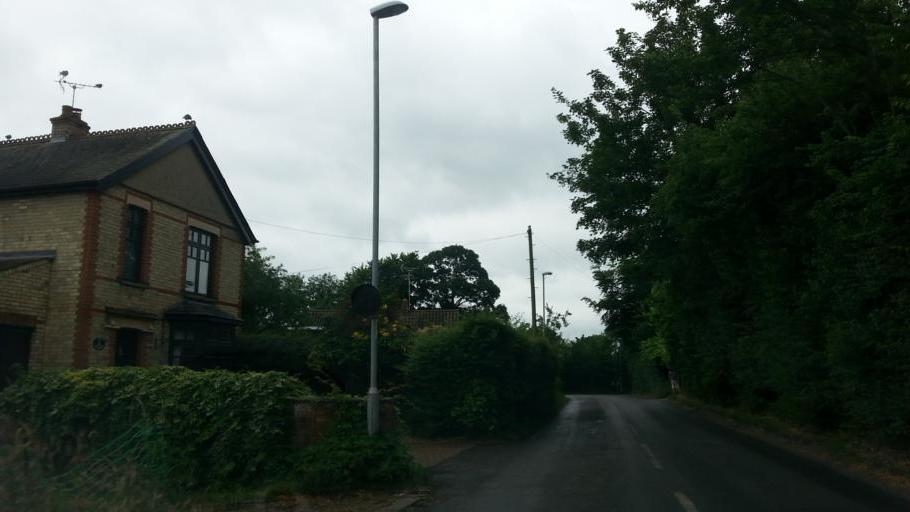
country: GB
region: England
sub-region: Cambridgeshire
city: Histon
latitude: 52.2493
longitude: 0.1209
